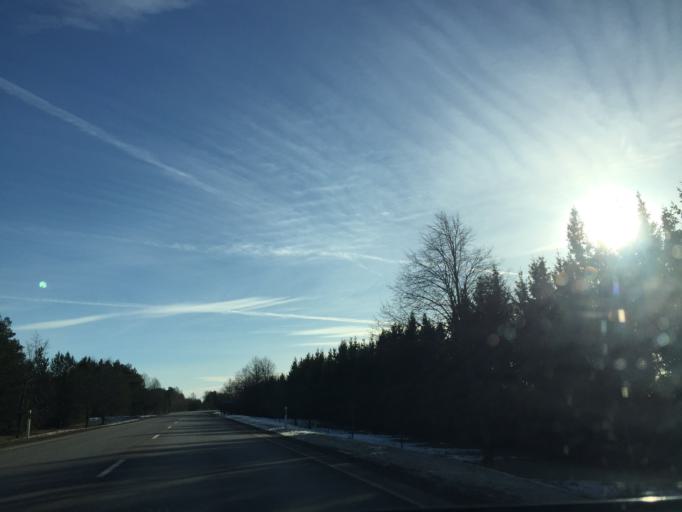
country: EE
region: Saare
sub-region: Orissaare vald
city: Orissaare
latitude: 58.5765
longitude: 23.1660
